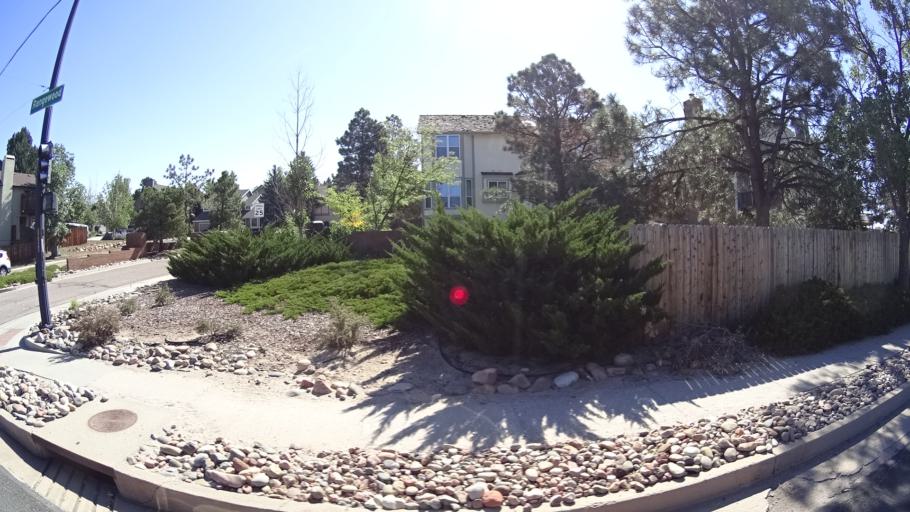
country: US
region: Colorado
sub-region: El Paso County
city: Black Forest
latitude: 38.9428
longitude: -104.7557
